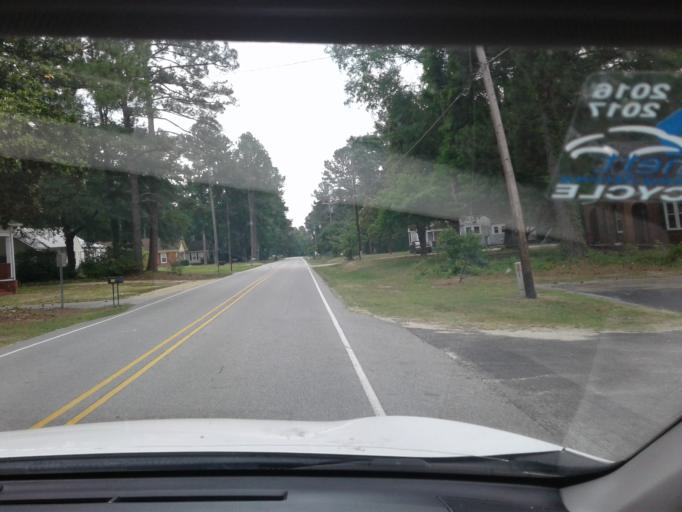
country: US
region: North Carolina
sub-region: Harnett County
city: Buies Creek
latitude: 35.4052
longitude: -78.7365
